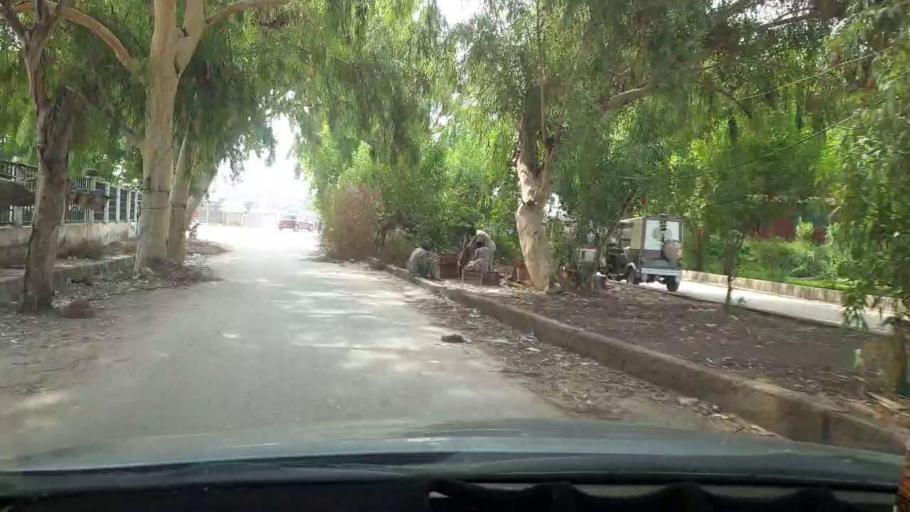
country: PK
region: Sindh
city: Khairpur
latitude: 27.5140
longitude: 68.7606
